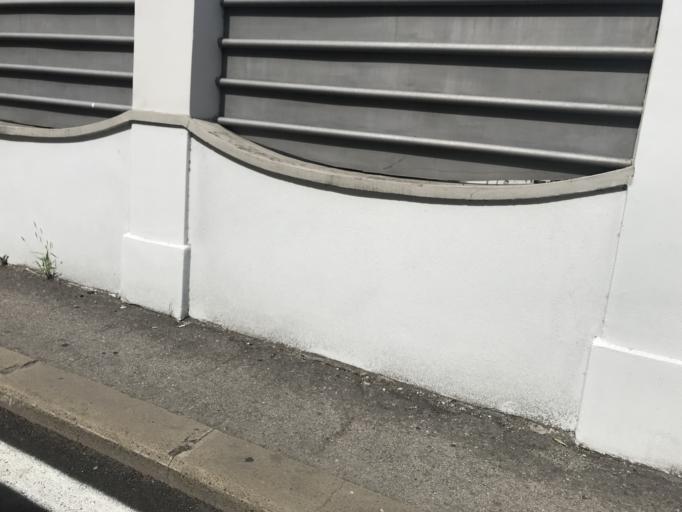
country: IT
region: Tuscany
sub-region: Province of Florence
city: Florence
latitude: 43.7737
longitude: 11.2222
